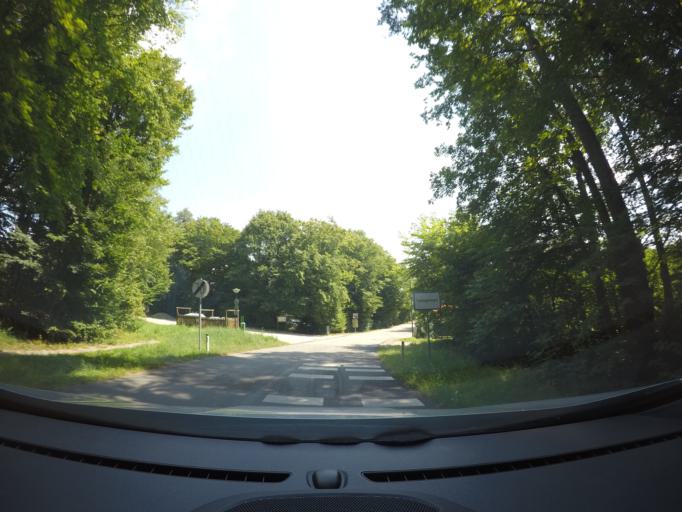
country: AT
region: Lower Austria
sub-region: Politischer Bezirk Tulln
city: Konigstetten
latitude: 48.2754
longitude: 16.1505
